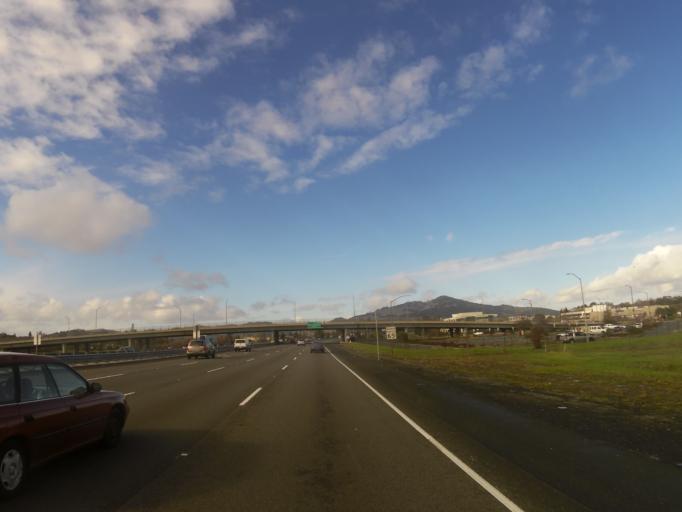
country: US
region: California
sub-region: Marin County
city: Novato
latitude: 38.0909
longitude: -122.5575
